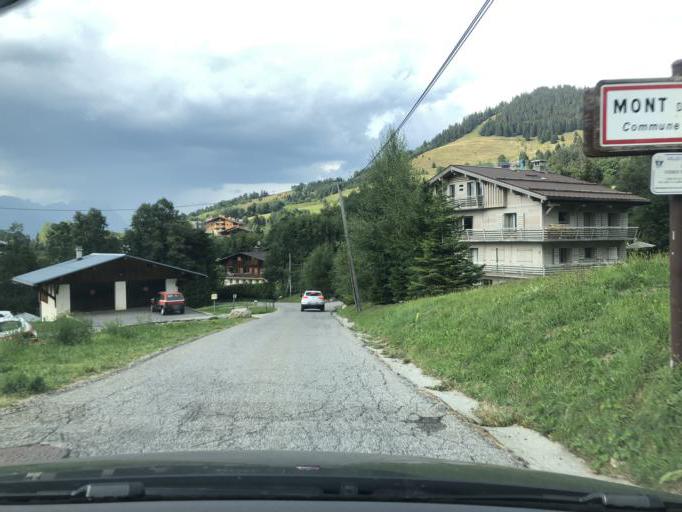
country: FR
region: Rhone-Alpes
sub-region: Departement de la Haute-Savoie
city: Megeve
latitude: 45.8436
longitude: 6.6430
